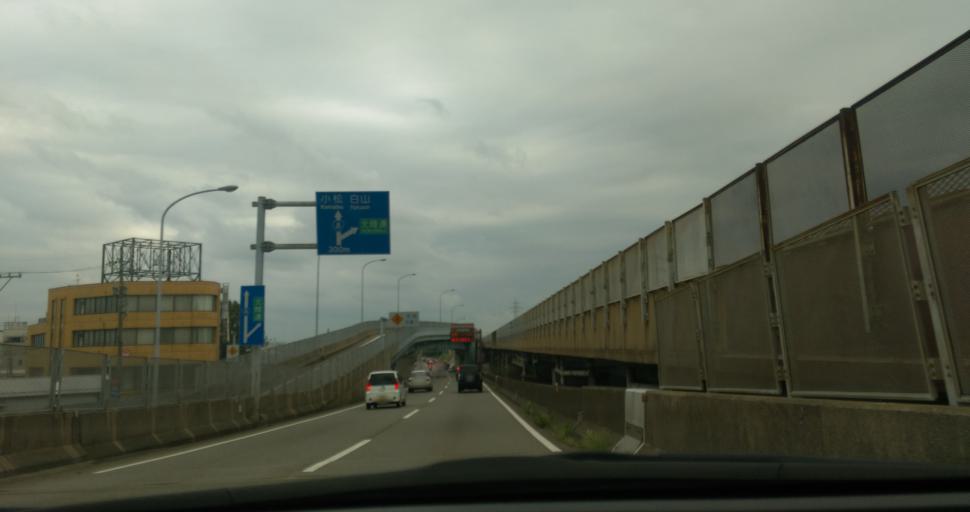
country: JP
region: Ishikawa
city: Kanazawa-shi
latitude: 36.5677
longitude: 136.6013
